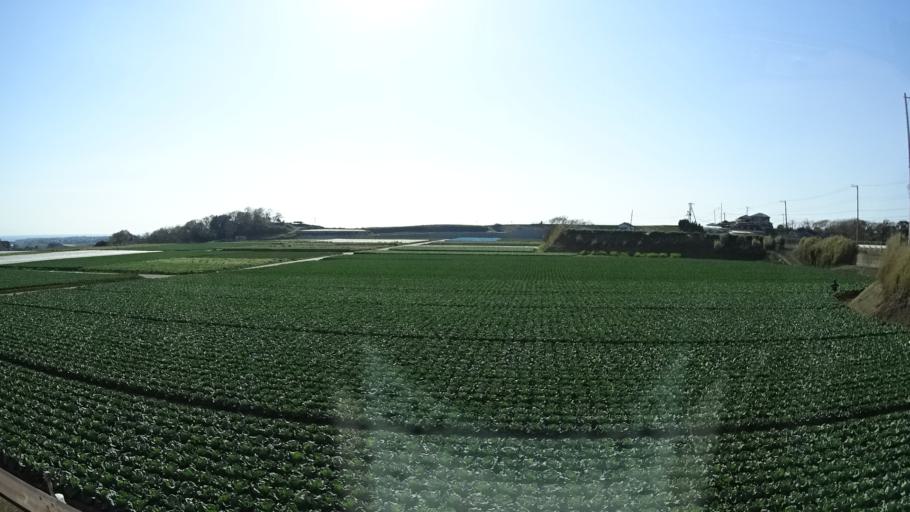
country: JP
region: Kanagawa
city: Miura
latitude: 35.1560
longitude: 139.6460
